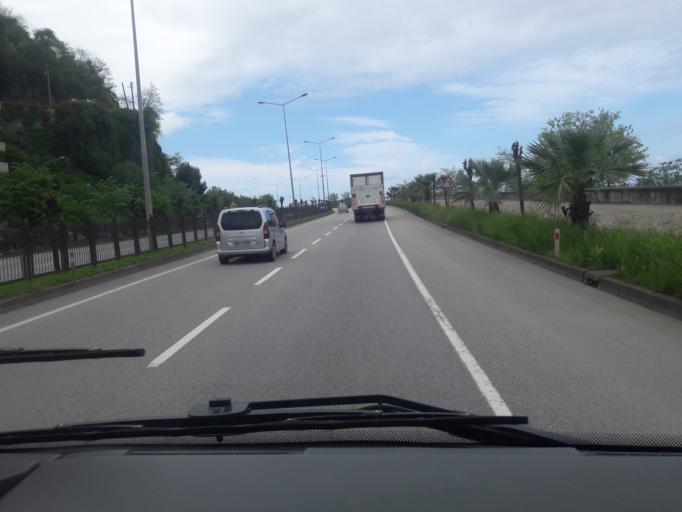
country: TR
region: Giresun
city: Giresun
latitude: 40.9187
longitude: 38.3953
